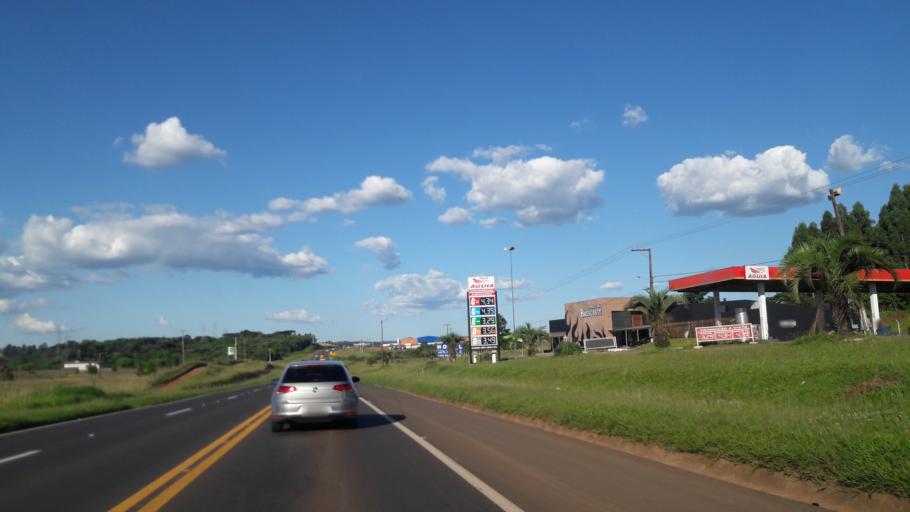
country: BR
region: Parana
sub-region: Guarapuava
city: Guarapuava
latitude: -25.3767
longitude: -51.5047
